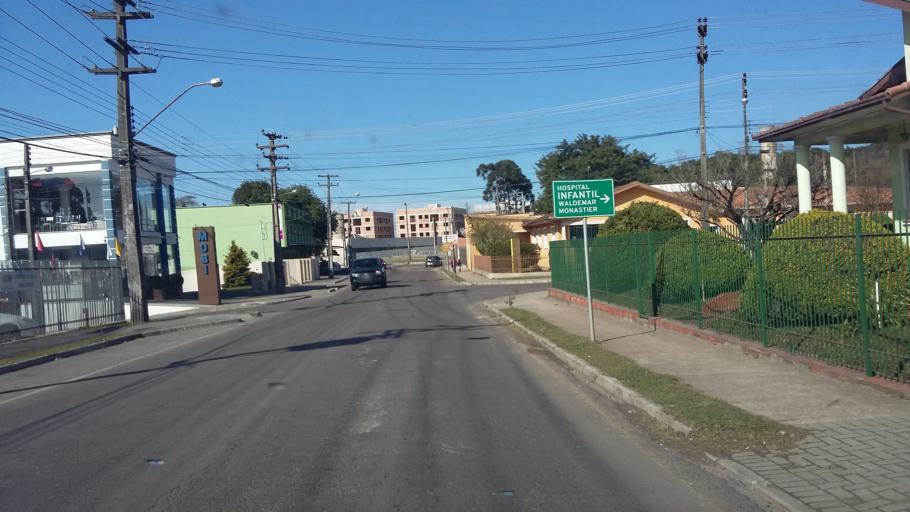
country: BR
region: Parana
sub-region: Campo Largo
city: Campo Largo
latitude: -25.4530
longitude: -49.5416
